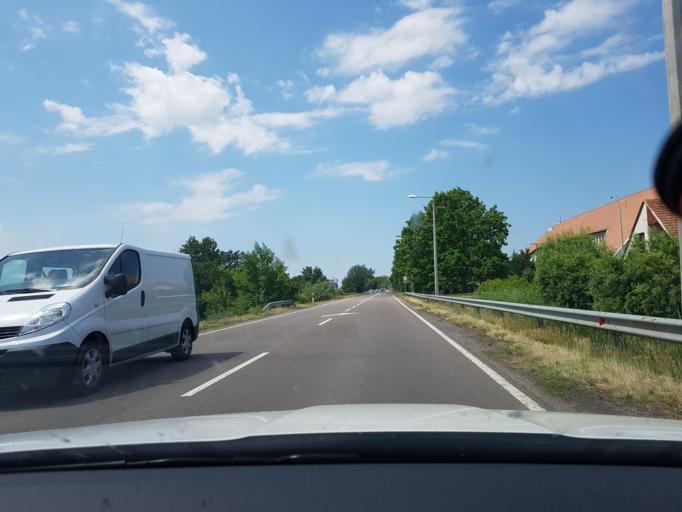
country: HU
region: Hajdu-Bihar
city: Hortobagy
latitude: 47.5817
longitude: 21.1580
